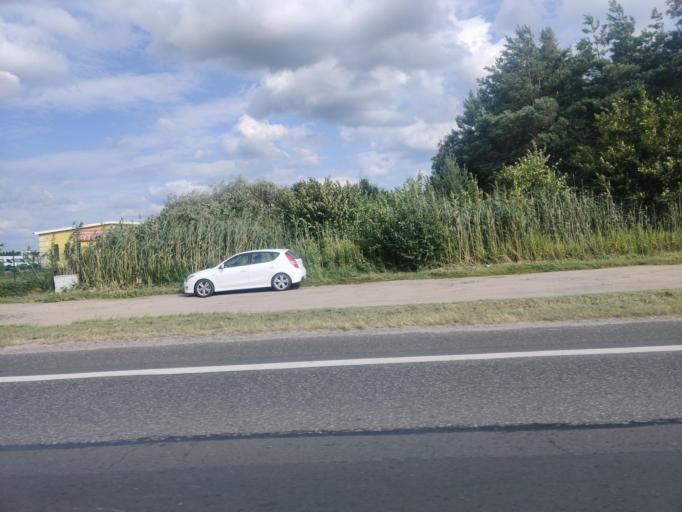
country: PL
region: Greater Poland Voivodeship
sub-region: Konin
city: Konin
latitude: 52.1952
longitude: 18.2677
